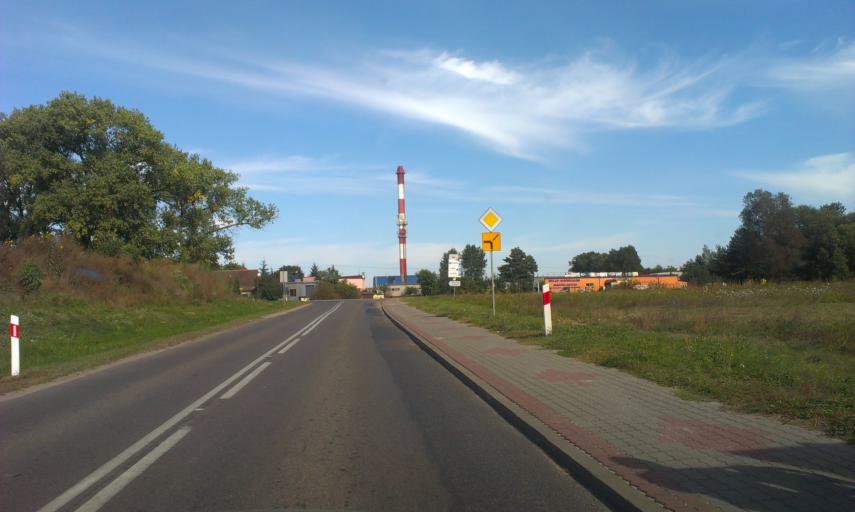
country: PL
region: Greater Poland Voivodeship
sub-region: Powiat zlotowski
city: Zlotow
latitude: 53.3532
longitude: 17.0503
